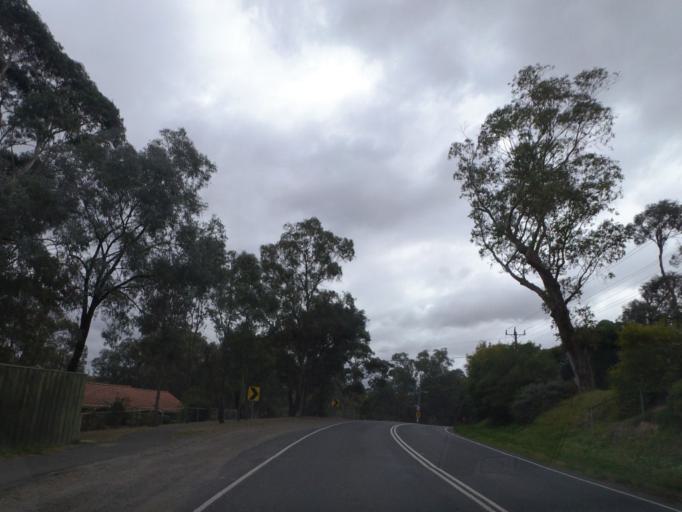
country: AU
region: Victoria
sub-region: Nillumbik
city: North Warrandyte
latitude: -37.7430
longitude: 145.2107
